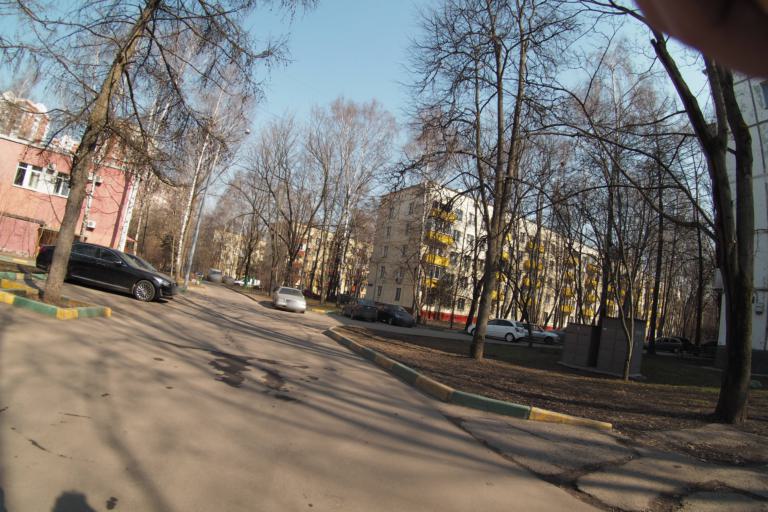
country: RU
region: Moscow
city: Matveyevskoye
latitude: 55.7107
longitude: 37.4852
